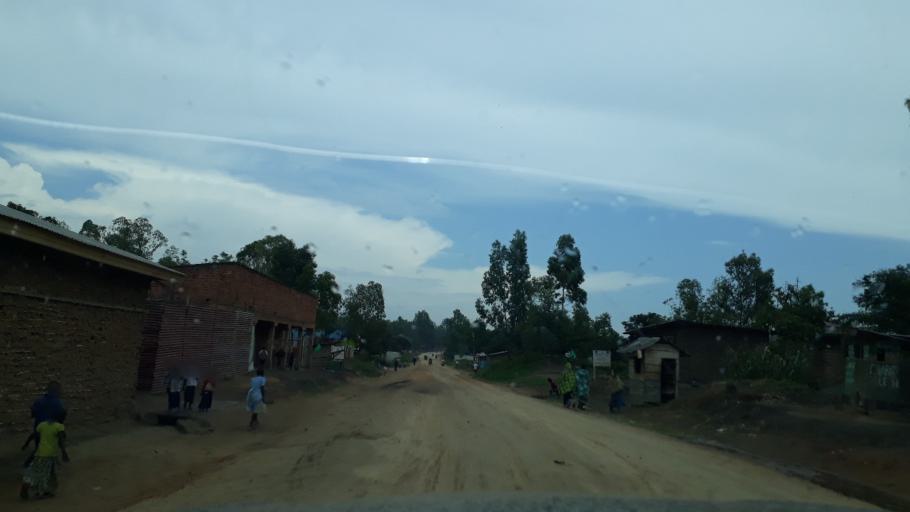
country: CD
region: Eastern Province
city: Bunia
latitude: 1.5965
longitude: 30.2641
